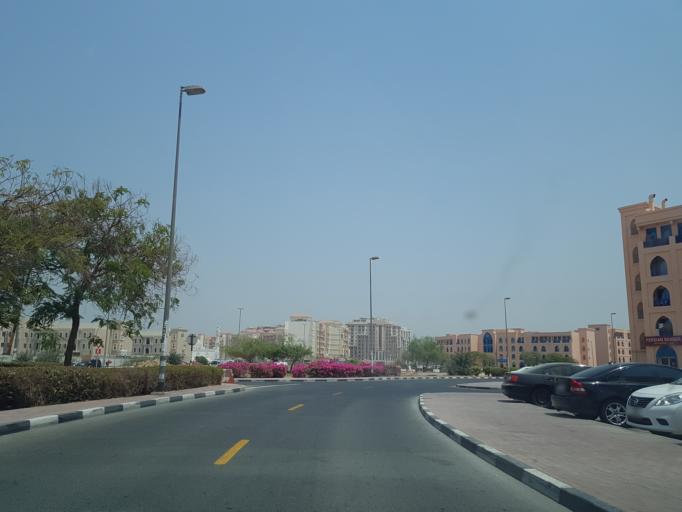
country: AE
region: Ash Shariqah
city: Sharjah
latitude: 25.1589
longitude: 55.4068
